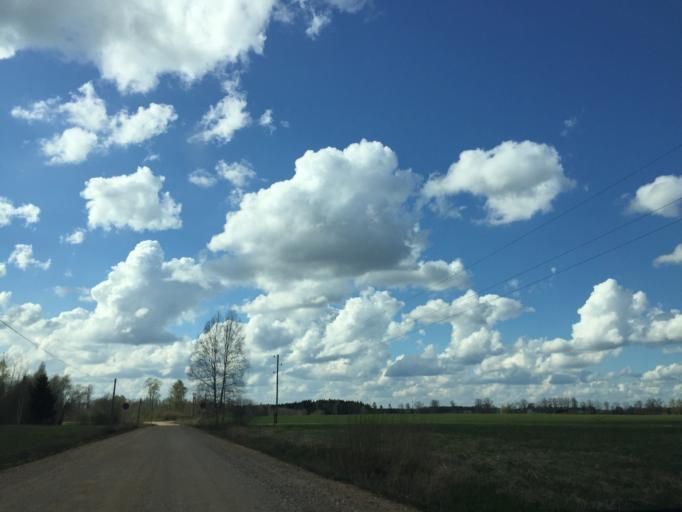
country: LV
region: Beverina
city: Murmuiza
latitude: 57.4743
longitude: 25.5115
